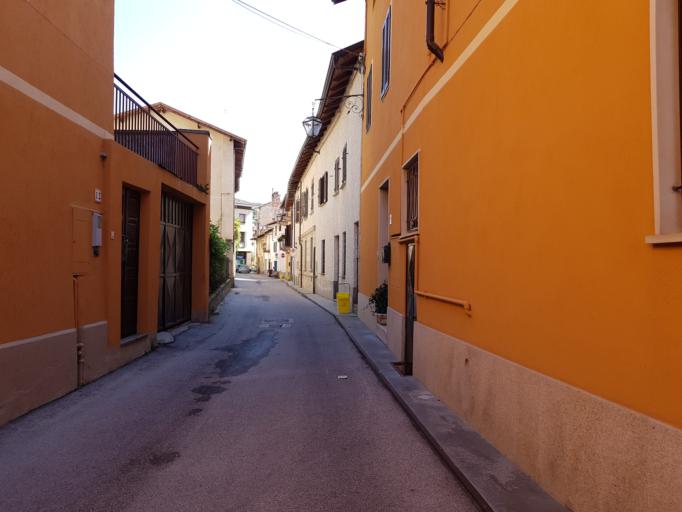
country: IT
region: Piedmont
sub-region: Provincia di Cuneo
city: Dronero
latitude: 44.4667
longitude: 7.3589
